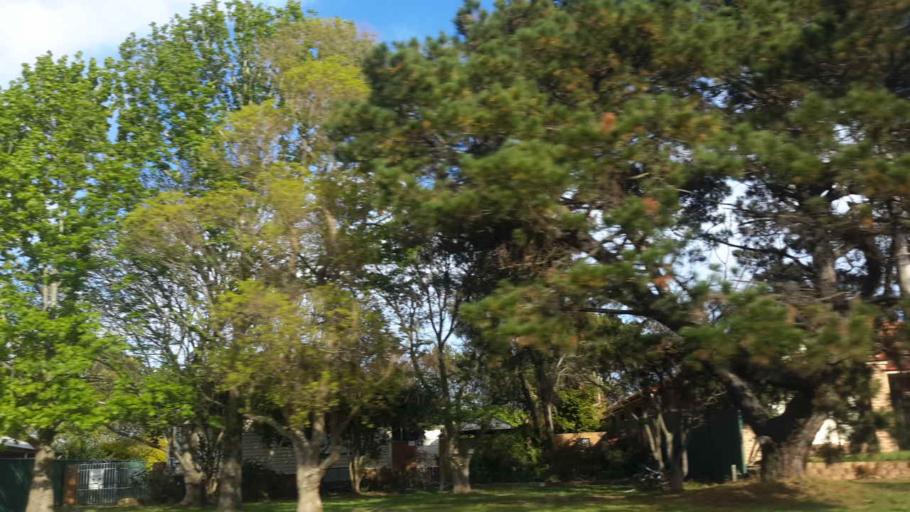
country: AU
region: New South Wales
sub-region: Wollondilly
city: Douglas Park
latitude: -34.2027
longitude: 150.7867
